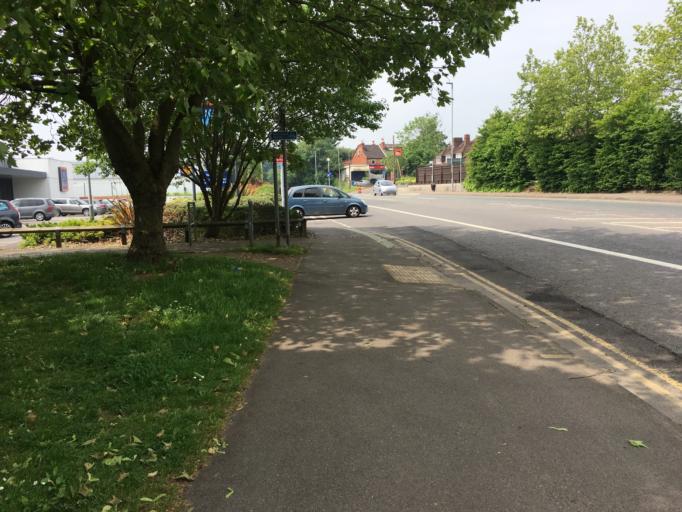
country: GB
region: England
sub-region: West Berkshire
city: Tilehurst
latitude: 51.4443
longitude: -1.0232
